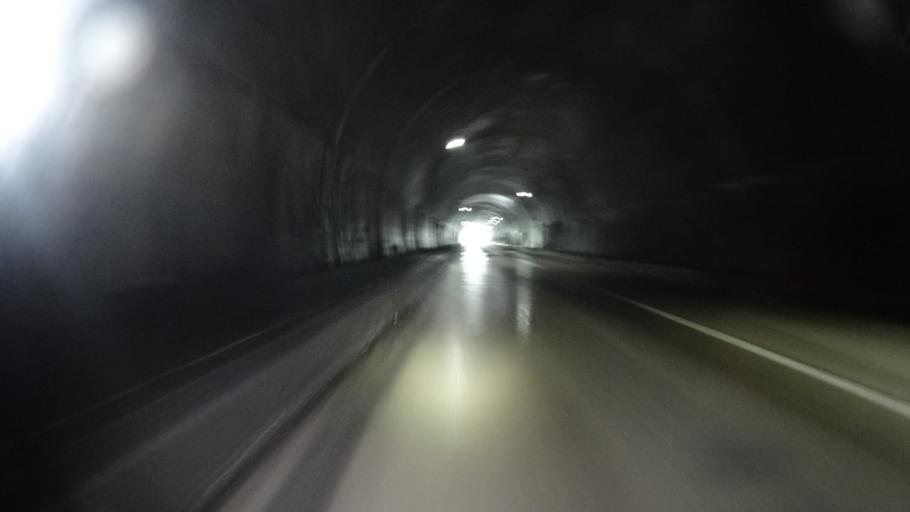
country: JP
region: Tokyo
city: Ome
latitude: 35.8338
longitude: 139.2095
